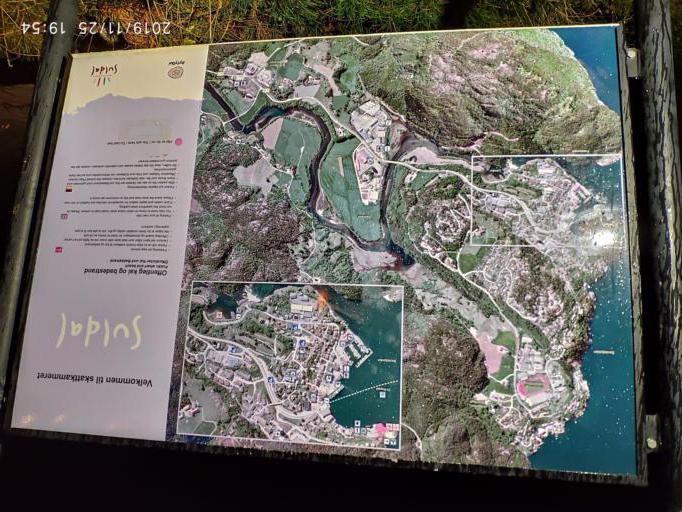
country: NO
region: Rogaland
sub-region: Suldal
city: Sand
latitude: 59.4851
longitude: 6.2467
